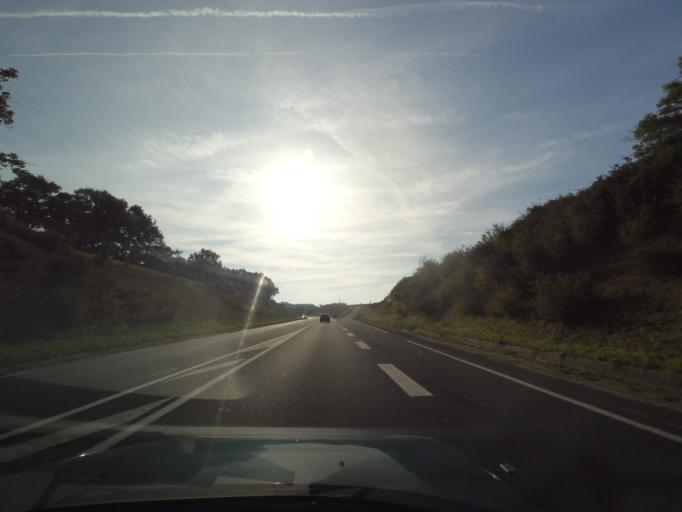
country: FR
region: Pays de la Loire
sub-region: Departement de la Vendee
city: Bouffere
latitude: 46.9624
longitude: -1.3241
